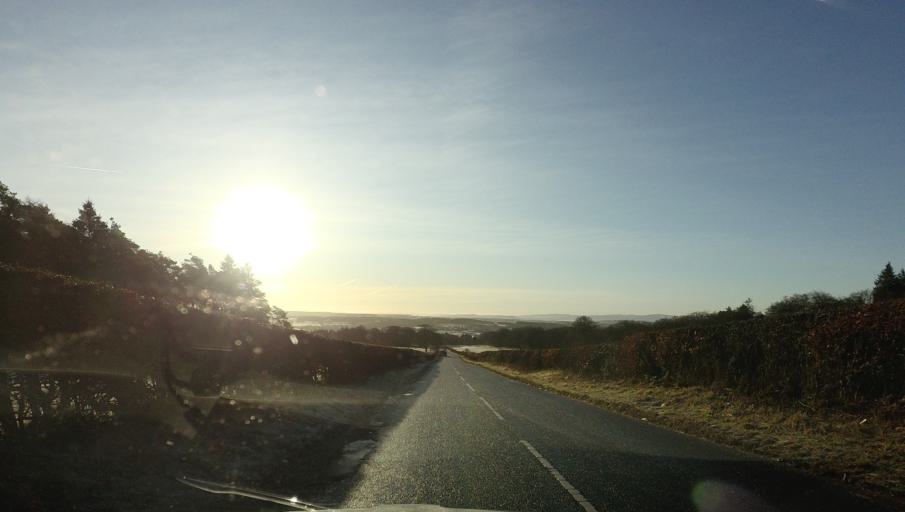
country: GB
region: Scotland
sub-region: North Lanarkshire
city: Shotts
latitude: 55.8222
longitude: -3.8347
